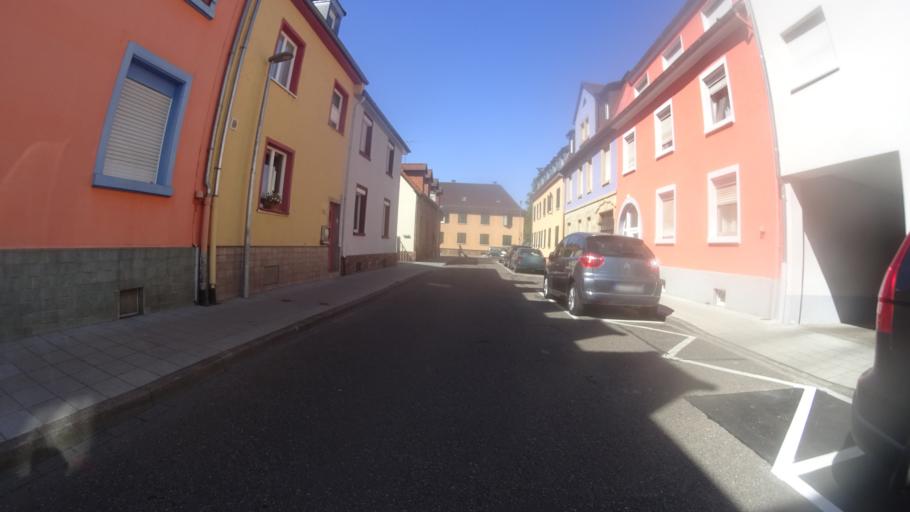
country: DE
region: Baden-Wuerttemberg
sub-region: Karlsruhe Region
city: Karlsruhe
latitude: 49.0160
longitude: 8.4454
